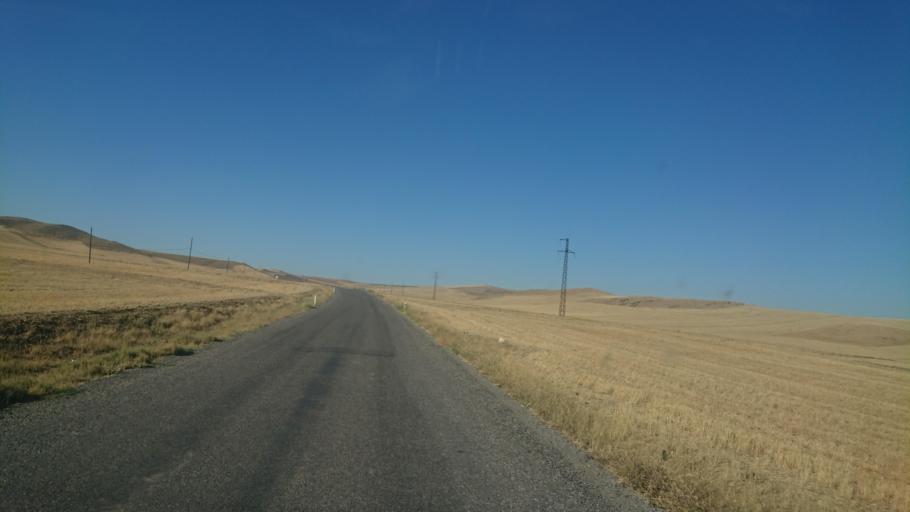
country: TR
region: Aksaray
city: Agacoren
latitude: 38.7803
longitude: 33.7094
